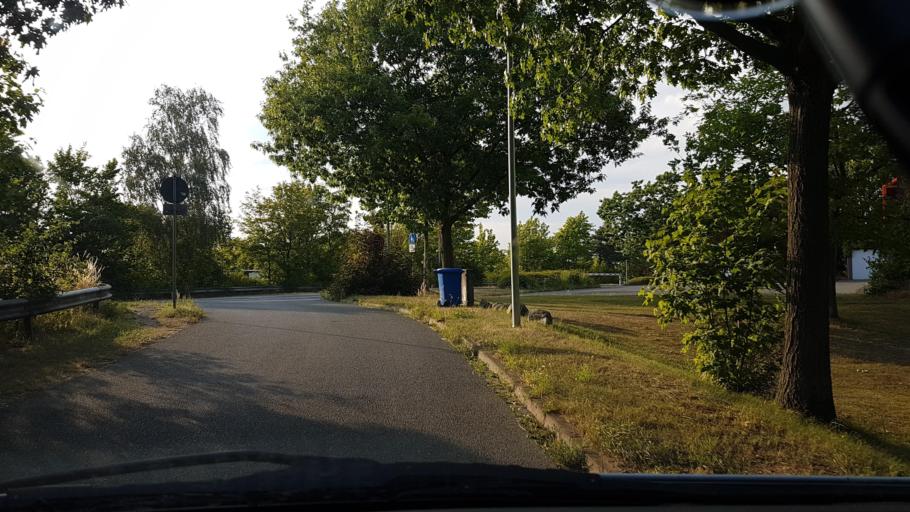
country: DE
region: Lower Saxony
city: Konigslutter am Elm
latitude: 52.2549
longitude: 10.8201
